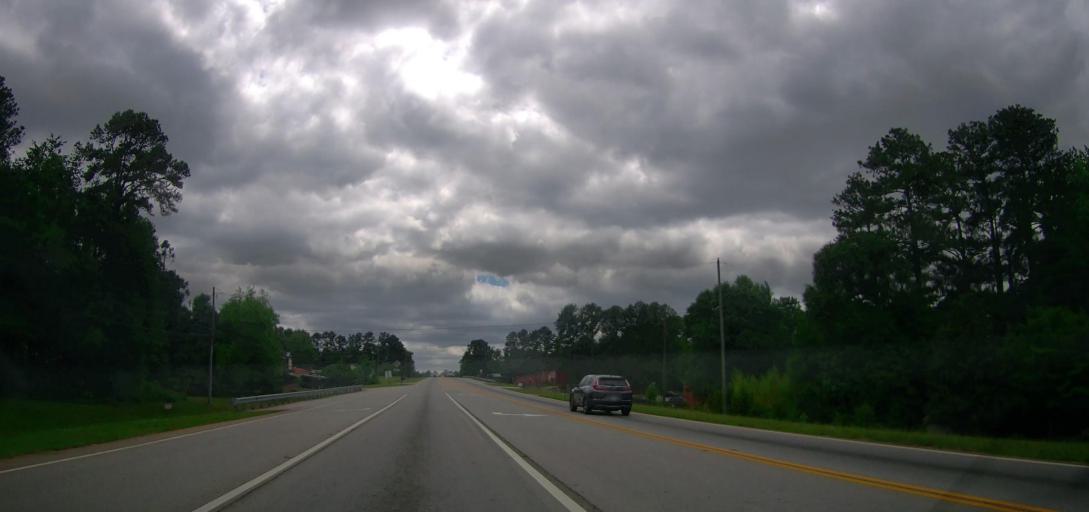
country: US
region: Georgia
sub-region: Henry County
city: Stockbridge
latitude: 33.5454
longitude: -84.1871
